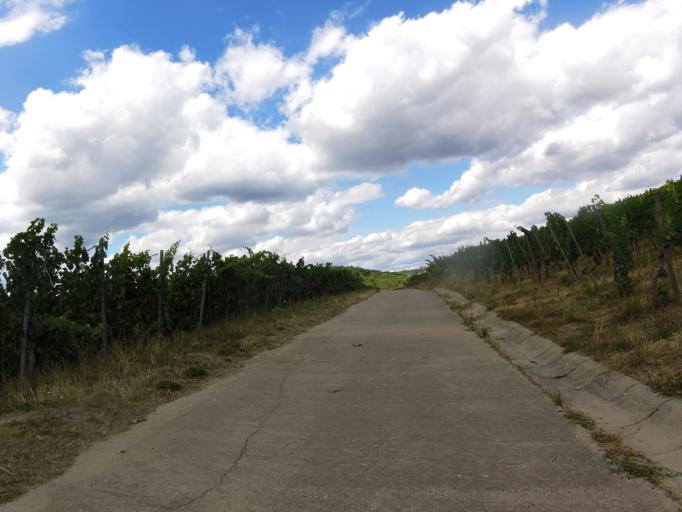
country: DE
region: Bavaria
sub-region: Regierungsbezirk Unterfranken
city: Eibelstadt
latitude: 49.7295
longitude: 10.0002
